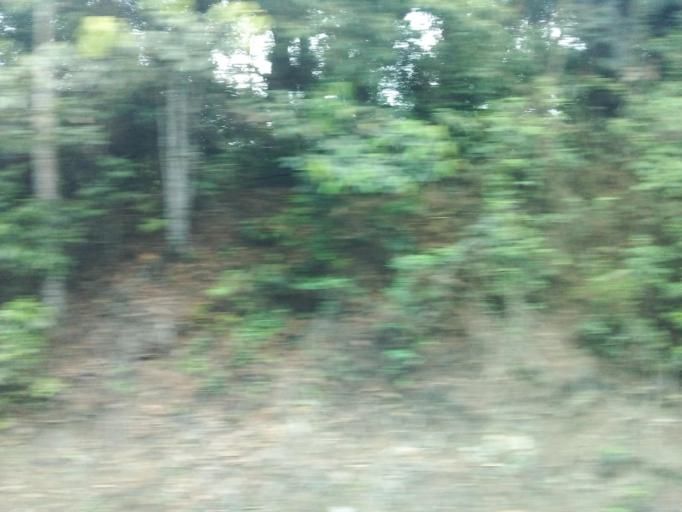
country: BR
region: Minas Gerais
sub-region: Rio Piracicaba
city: Rio Piracicaba
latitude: -19.9731
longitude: -43.2352
